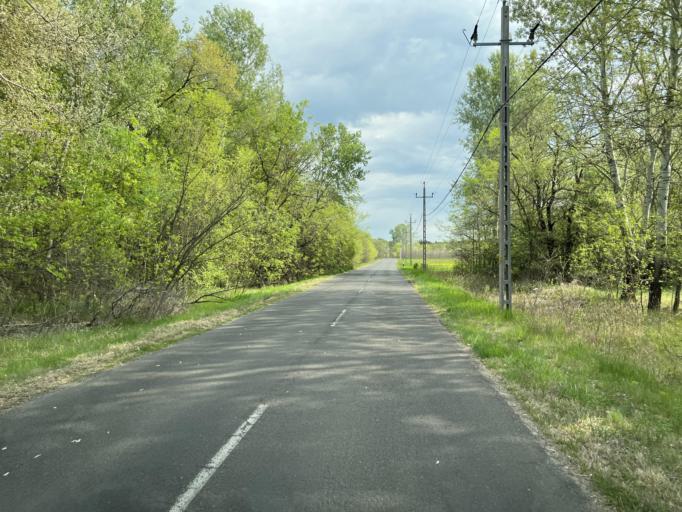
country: HU
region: Pest
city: Tapioszentmarton
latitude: 47.3535
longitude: 19.7902
